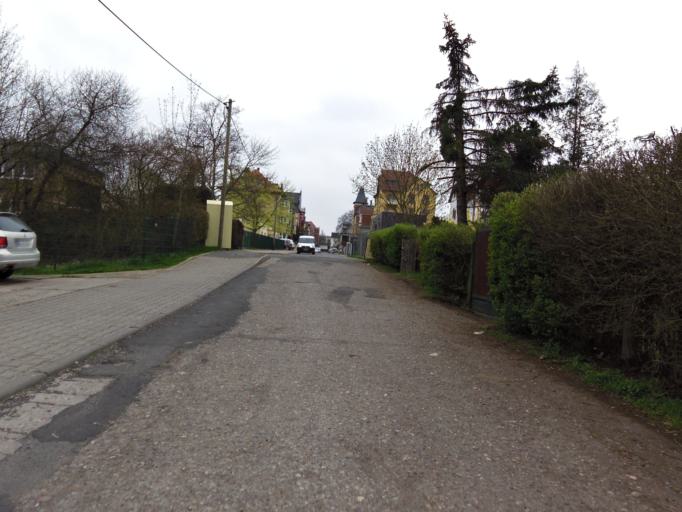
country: DE
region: Thuringia
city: Gotha
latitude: 50.9555
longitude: 10.6981
